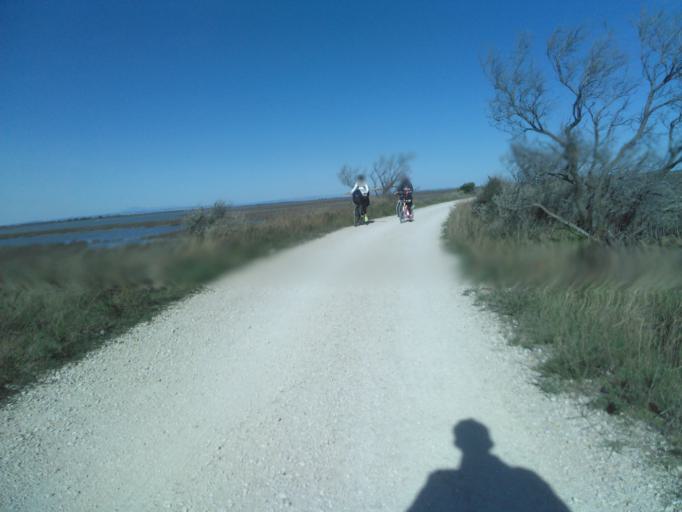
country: FR
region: Provence-Alpes-Cote d'Azur
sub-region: Departement des Bouches-du-Rhone
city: Saintes-Maries-de-la-Mer
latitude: 43.4614
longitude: 4.4980
